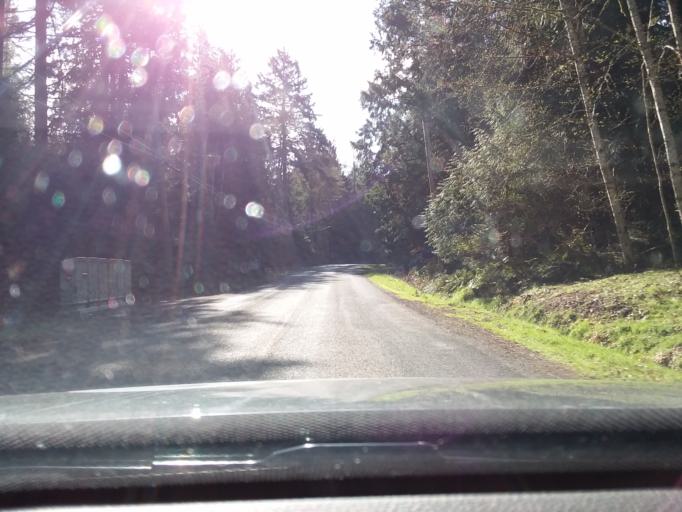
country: CA
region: British Columbia
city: North Cowichan
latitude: 48.9271
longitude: -123.4555
